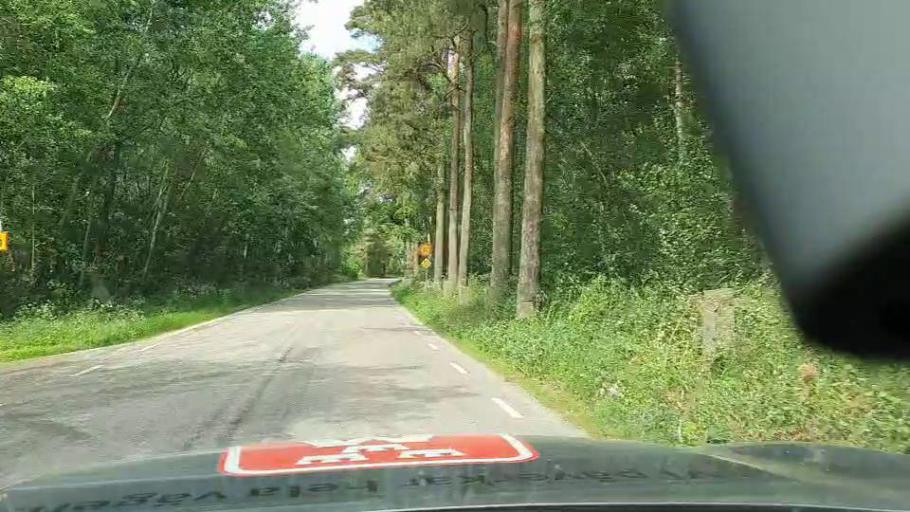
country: SE
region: Blekinge
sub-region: Karlshamns Kommun
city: Morrum
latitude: 56.1016
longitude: 14.6860
